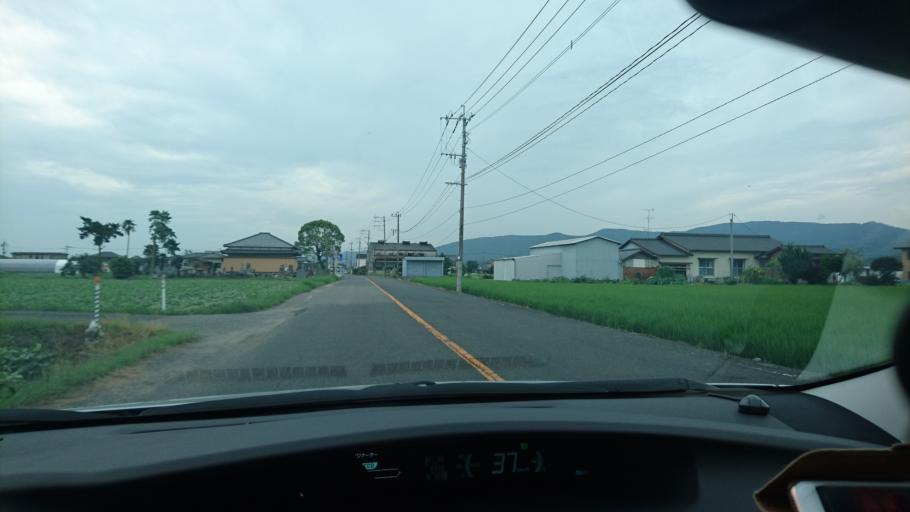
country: JP
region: Saga Prefecture
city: Kashima
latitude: 33.1972
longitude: 130.1148
